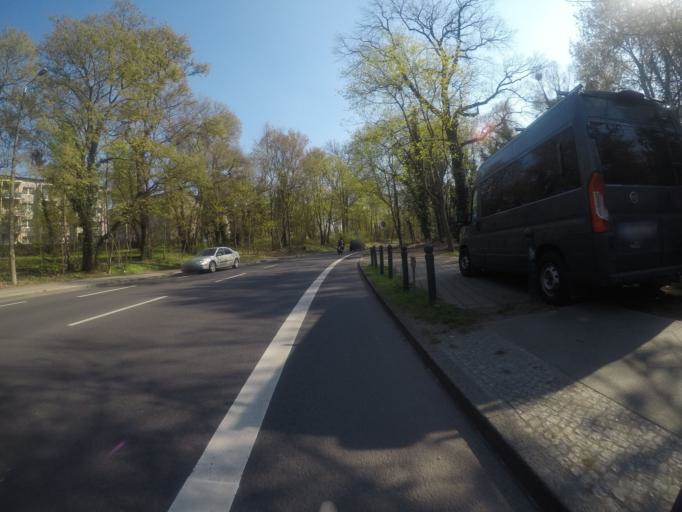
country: DE
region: Brandenburg
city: Potsdam
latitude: 52.4119
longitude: 13.0320
